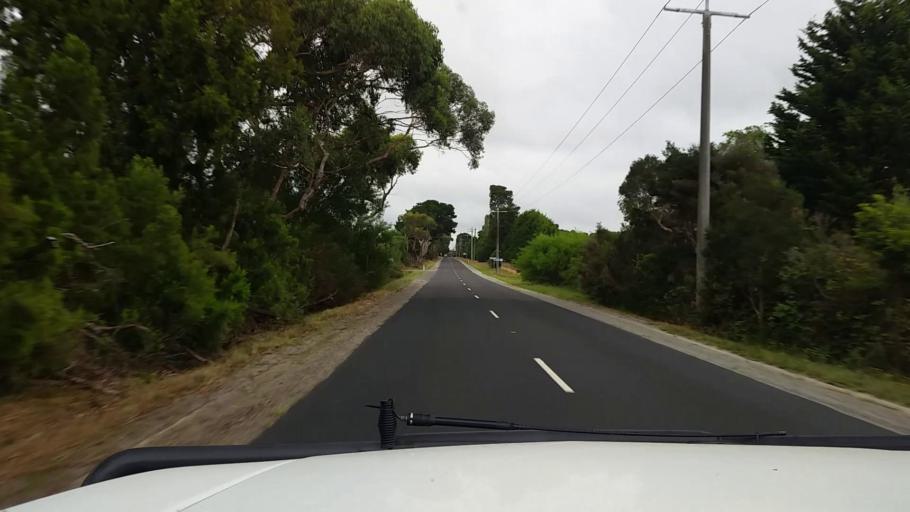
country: AU
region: Victoria
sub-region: Mornington Peninsula
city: Balnarring
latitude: -38.3438
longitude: 145.1457
